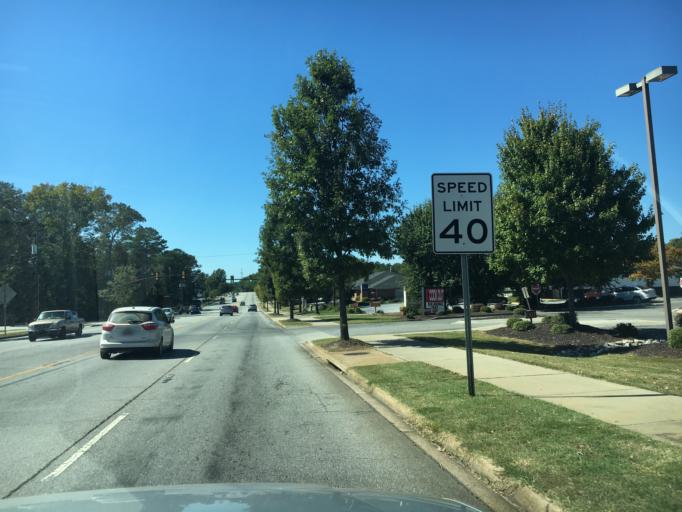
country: US
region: South Carolina
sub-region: Pickens County
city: Clemson
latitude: 34.6917
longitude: -82.8387
